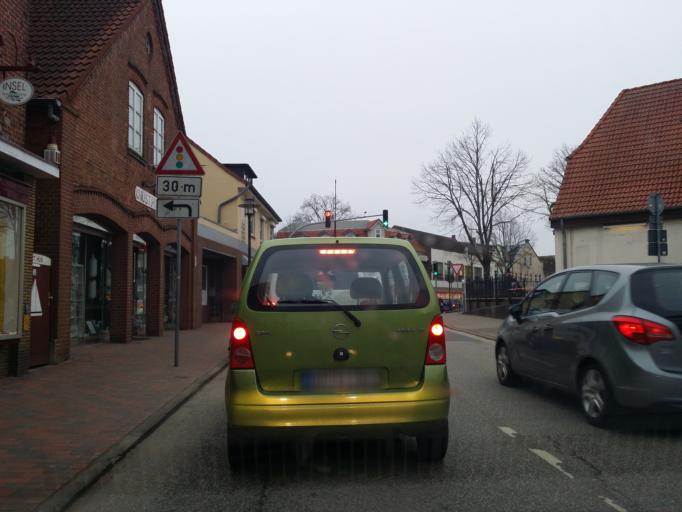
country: DE
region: Schleswig-Holstein
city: Fehmarn
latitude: 54.4404
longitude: 11.1974
